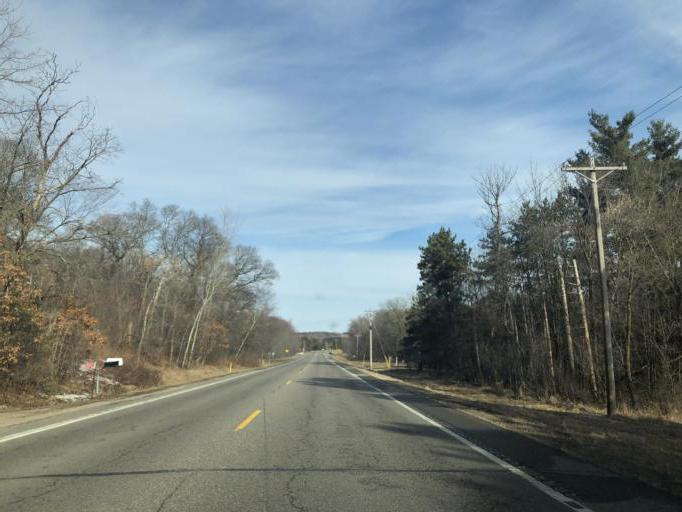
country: US
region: Minnesota
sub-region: Sherburne County
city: Becker
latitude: 45.4229
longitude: -93.8734
